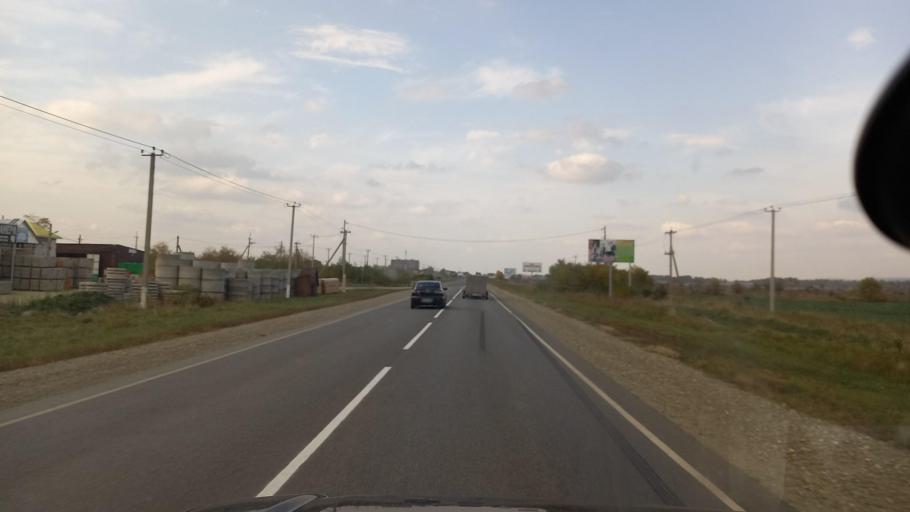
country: RU
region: Krasnodarskiy
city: Mostovskoy
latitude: 44.3823
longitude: 40.8205
